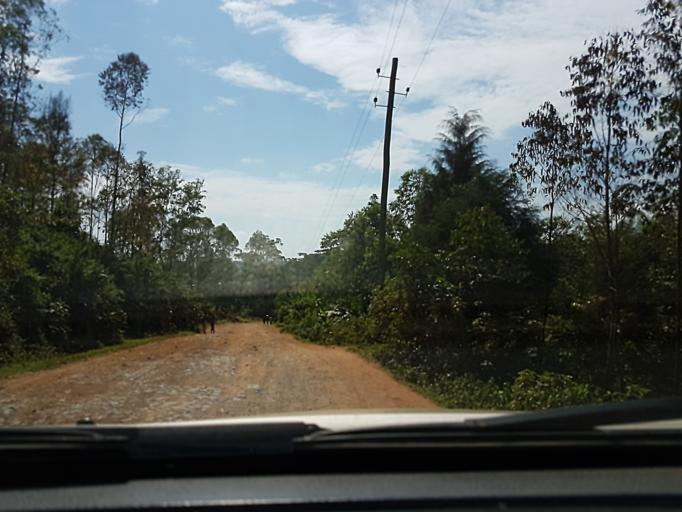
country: CD
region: South Kivu
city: Bukavu
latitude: -2.6528
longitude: 28.8730
